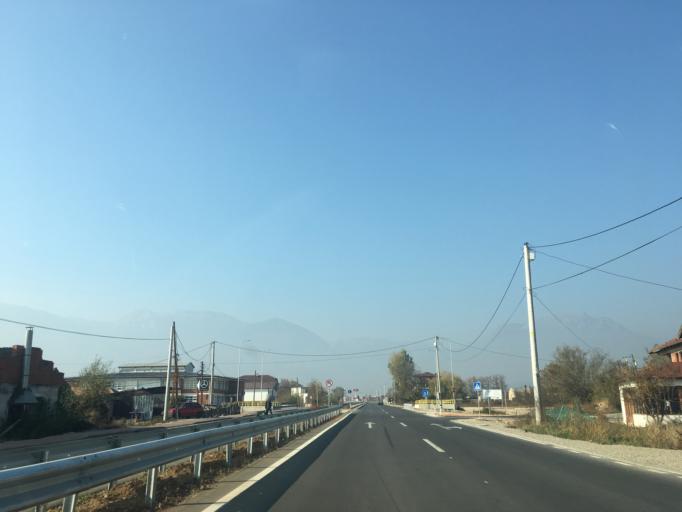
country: XK
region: Pec
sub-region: Komuna e Pejes
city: Dubova (Driloni)
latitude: 42.6584
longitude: 20.3512
